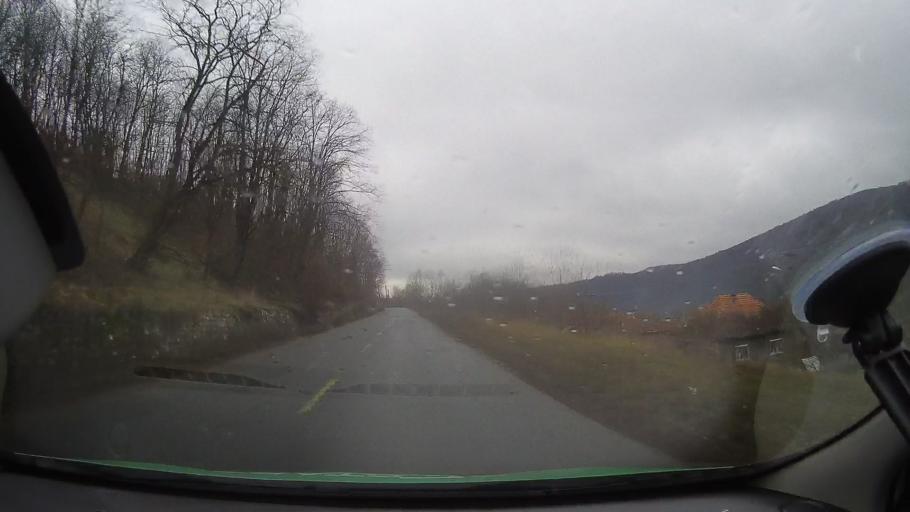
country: RO
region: Arad
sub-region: Comuna Halmagiu
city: Halmagiu
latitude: 46.2367
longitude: 22.5578
